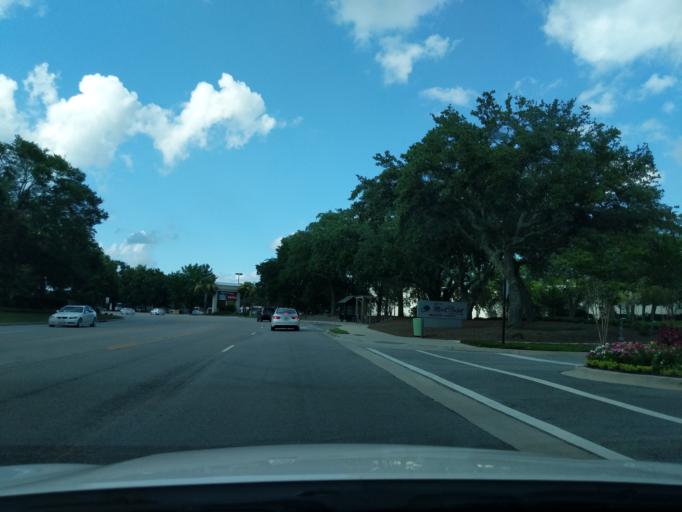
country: US
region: South Carolina
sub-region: Charleston County
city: Mount Pleasant
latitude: 32.8015
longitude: -79.8902
